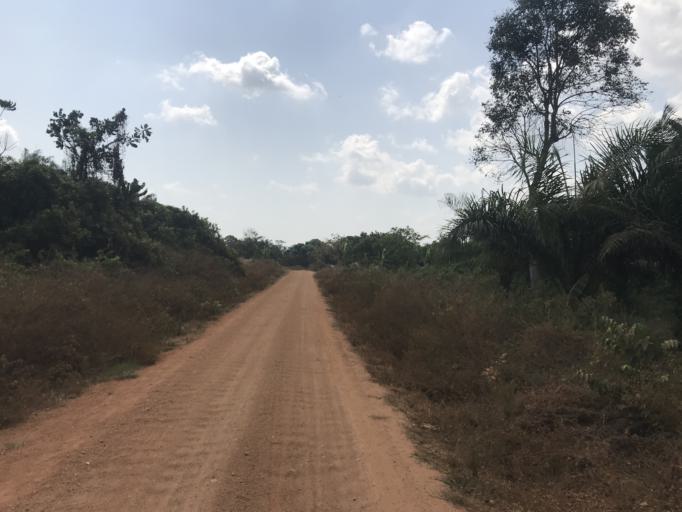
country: NG
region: Osun
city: Ifon
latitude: 7.9707
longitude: 4.5089
